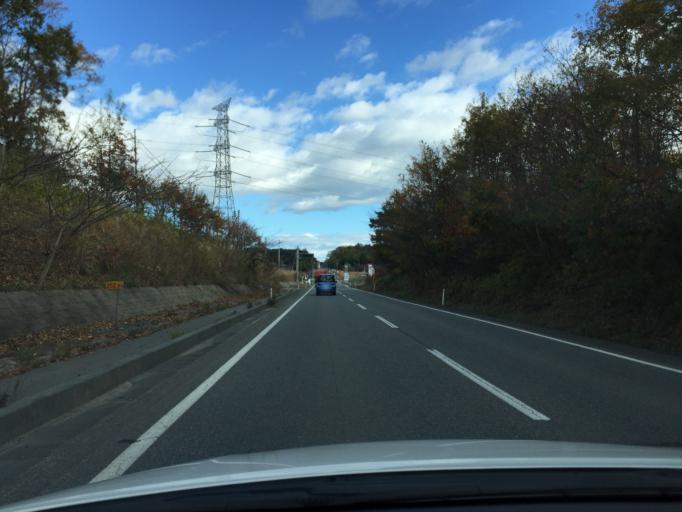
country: JP
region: Fukushima
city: Namie
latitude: 37.4243
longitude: 141.0047
